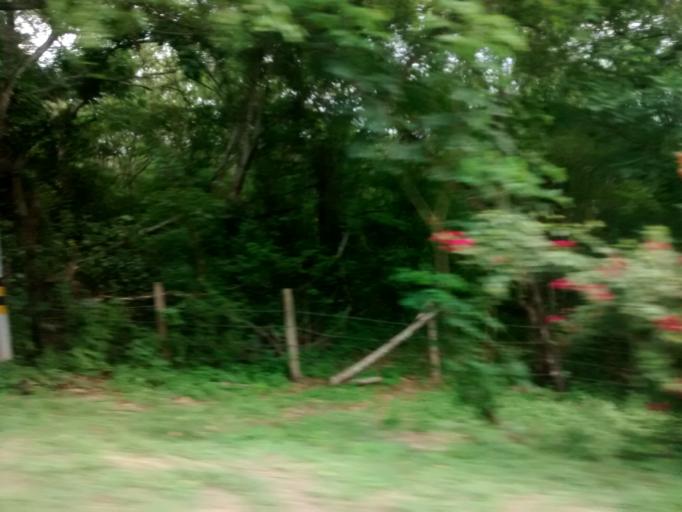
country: CO
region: Cundinamarca
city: Ricaurte
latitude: 4.2492
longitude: -74.7310
